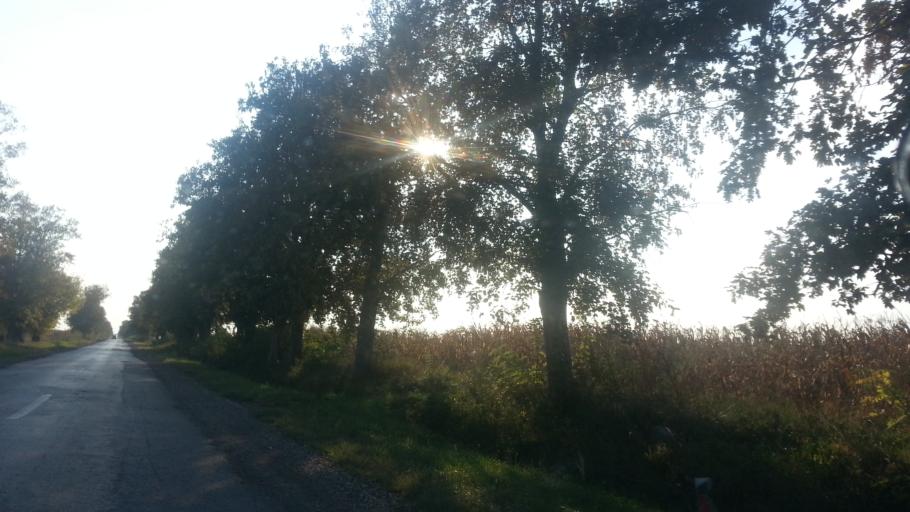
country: RS
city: Novi Karlovci
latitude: 45.1008
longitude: 20.2060
